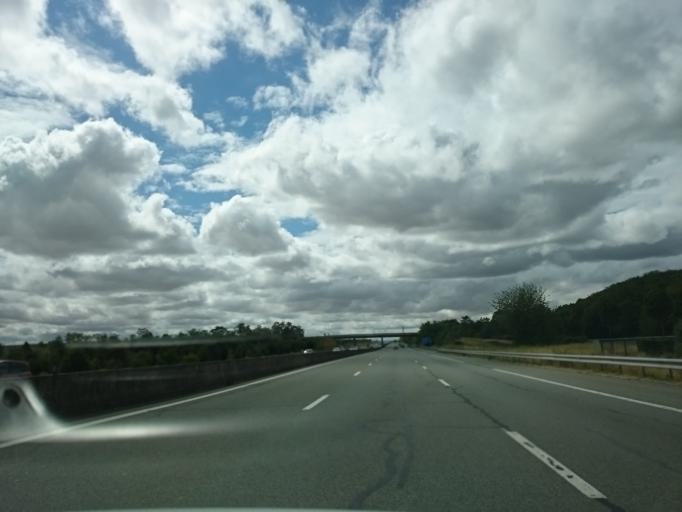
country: FR
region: Centre
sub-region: Departement d'Eure-et-Loir
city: Gasville-Oiseme
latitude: 48.4487
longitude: 1.5332
